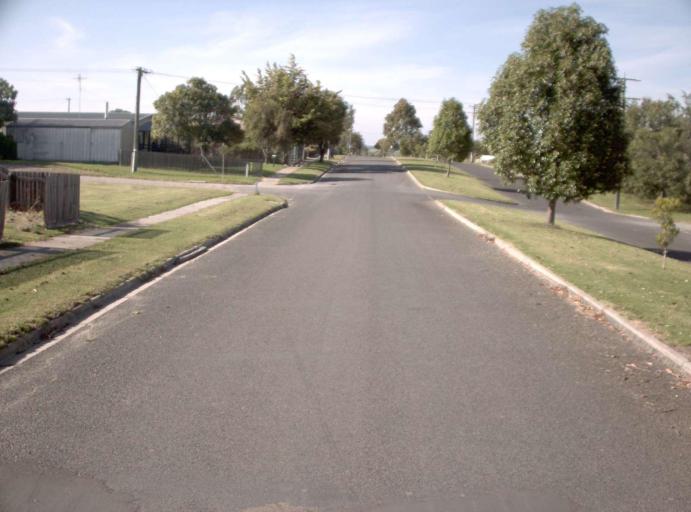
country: AU
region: Victoria
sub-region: East Gippsland
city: Lakes Entrance
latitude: -37.6952
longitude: 148.4578
